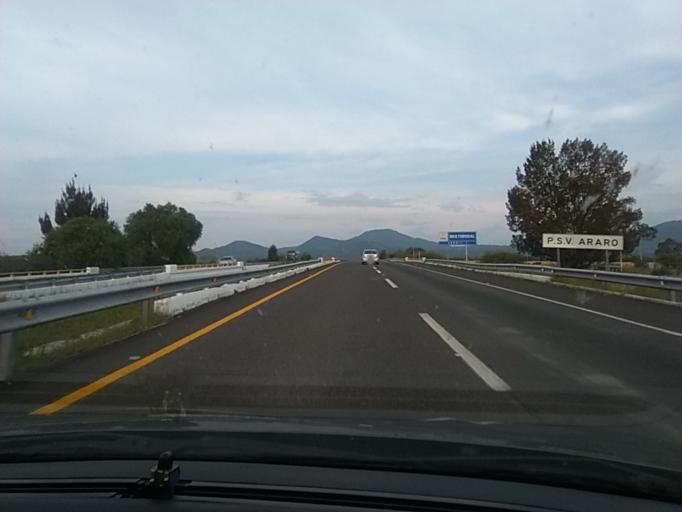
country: MX
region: Michoacan
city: Zinapecuaro
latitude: 19.9018
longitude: -100.8093
